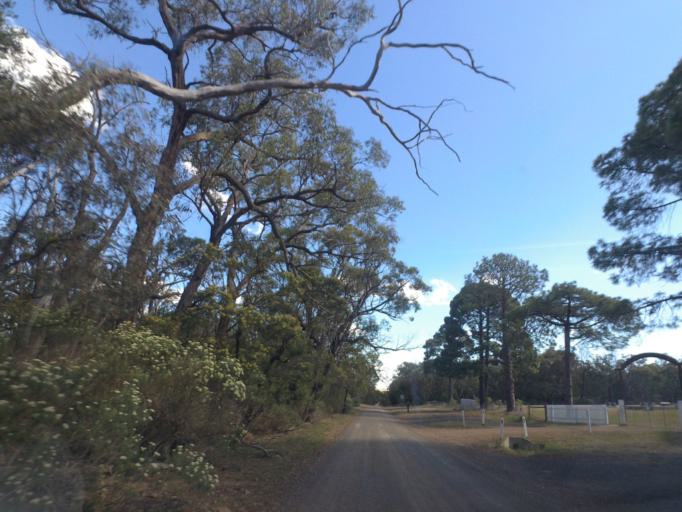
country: AU
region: Victoria
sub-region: Hume
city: Sunbury
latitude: -37.4455
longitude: 144.6637
